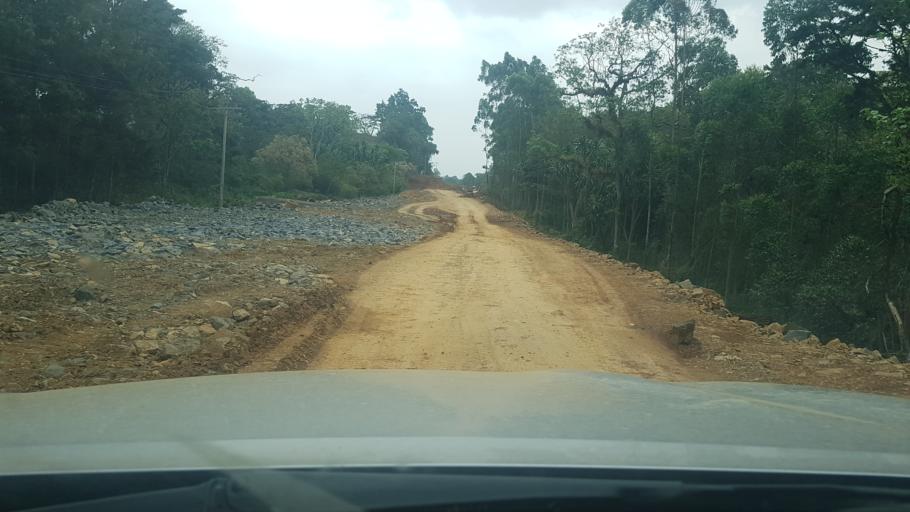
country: ET
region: Oromiya
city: Gore
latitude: 7.9016
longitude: 35.4994
